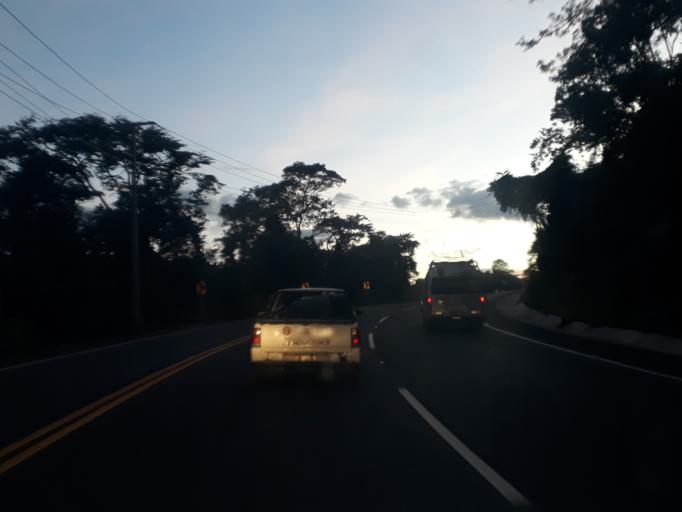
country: NI
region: Managua
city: El Crucero
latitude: 12.0124
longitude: -86.3160
